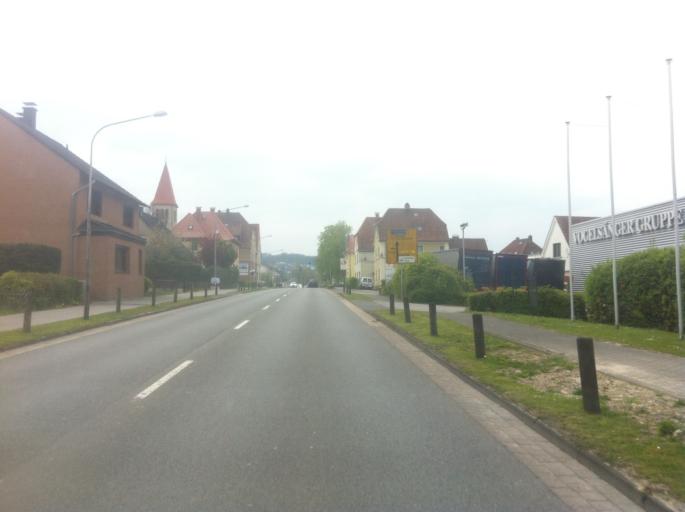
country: DE
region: North Rhine-Westphalia
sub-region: Regierungsbezirk Detmold
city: Leopoldshohe
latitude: 51.9704
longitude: 8.7139
